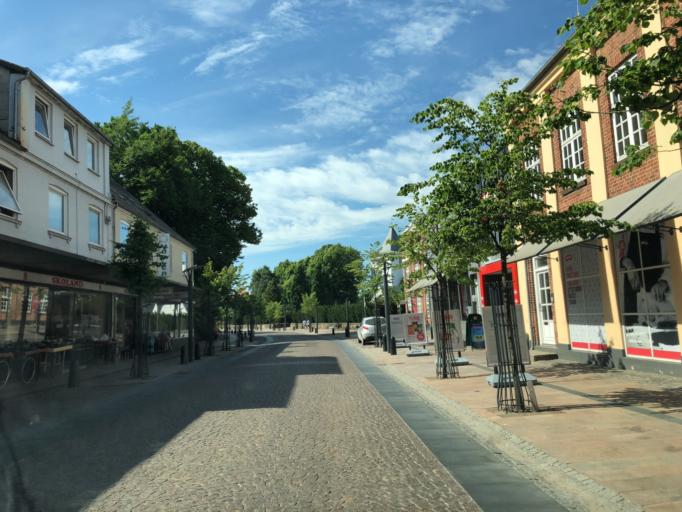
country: DK
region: Central Jutland
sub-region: Ikast-Brande Kommune
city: Brande
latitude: 55.9442
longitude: 9.1263
